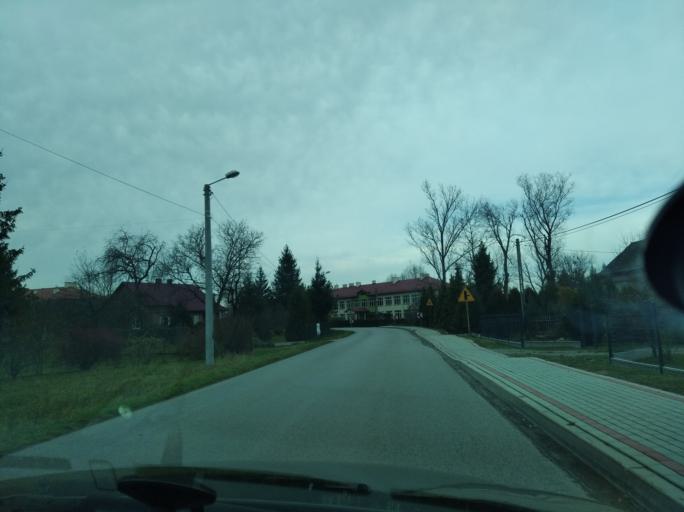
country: PL
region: Subcarpathian Voivodeship
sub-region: Powiat lancucki
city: Rogozno
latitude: 50.0996
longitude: 22.4019
